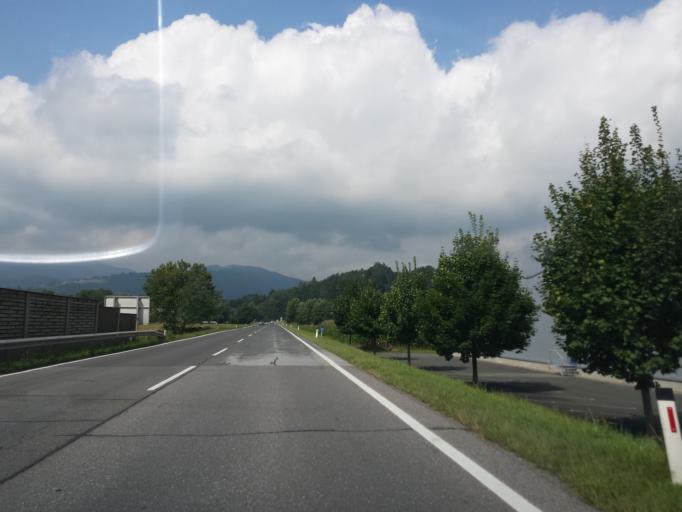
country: AT
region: Styria
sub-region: Politischer Bezirk Deutschlandsberg
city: Deutschlandsberg
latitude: 46.8309
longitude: 15.2520
